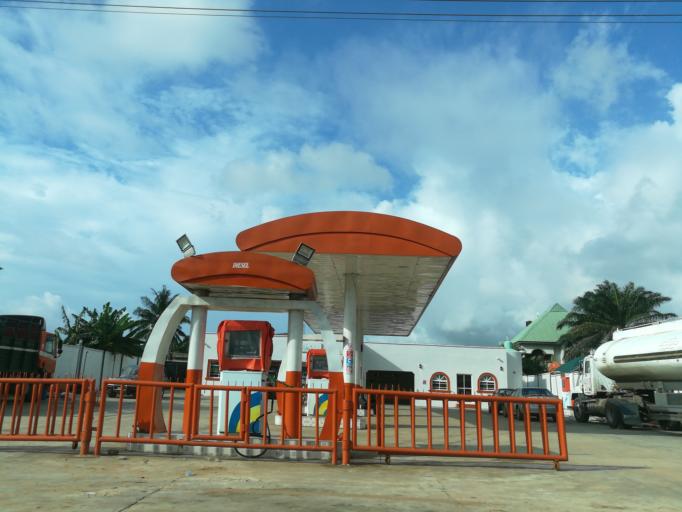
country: NG
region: Lagos
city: Ebute Ikorodu
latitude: 6.5980
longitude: 3.4986
